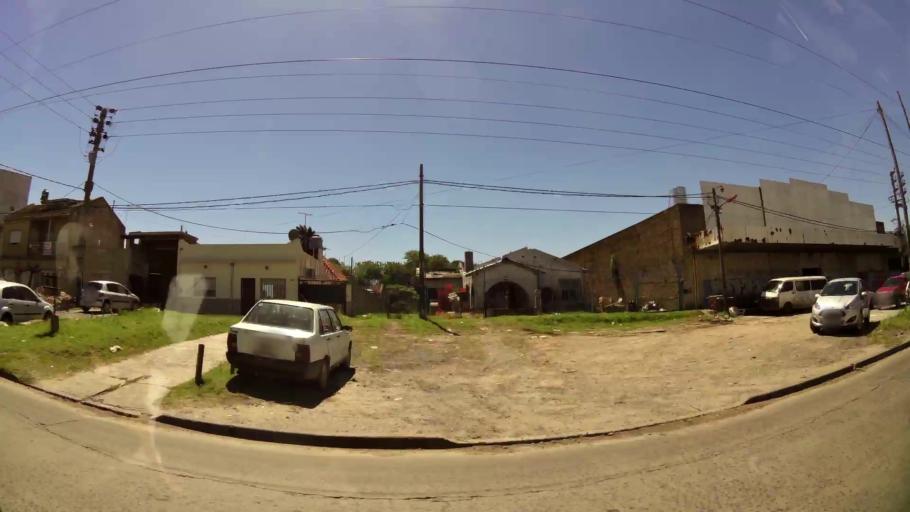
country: AR
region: Buenos Aires
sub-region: Partido de Almirante Brown
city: Adrogue
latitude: -34.7528
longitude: -58.3443
